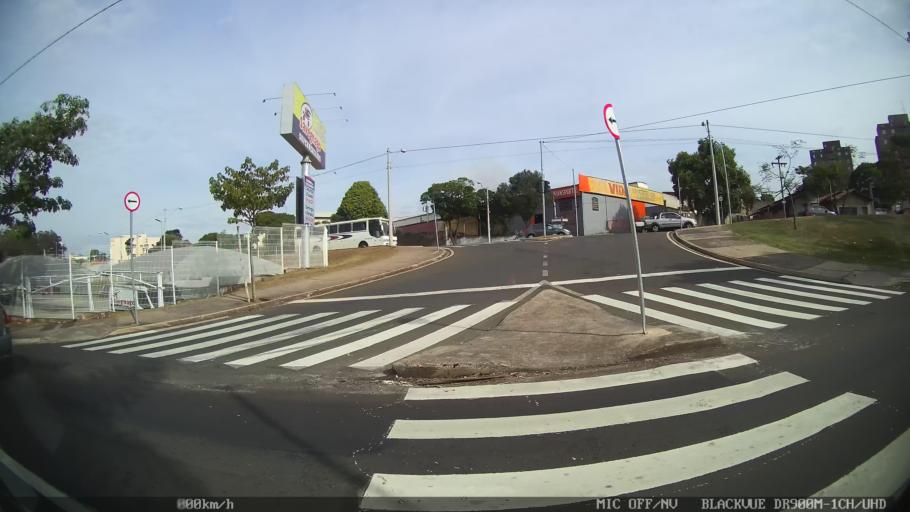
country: BR
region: Sao Paulo
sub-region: Piracicaba
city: Piracicaba
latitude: -22.7466
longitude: -47.6356
